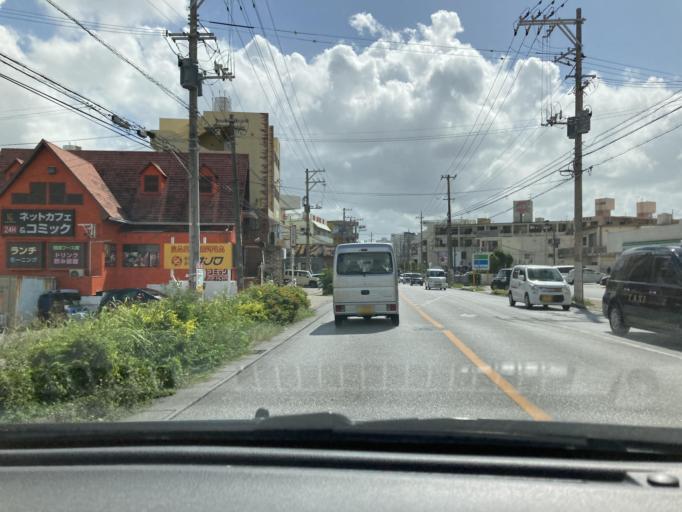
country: JP
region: Okinawa
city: Naha-shi
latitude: 26.2378
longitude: 127.7051
